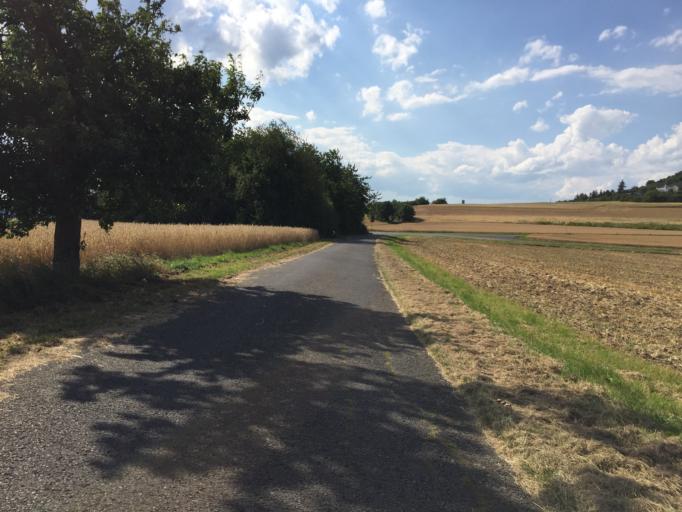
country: DE
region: Hesse
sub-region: Regierungsbezirk Giessen
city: Heuchelheim
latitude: 50.6078
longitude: 8.6401
